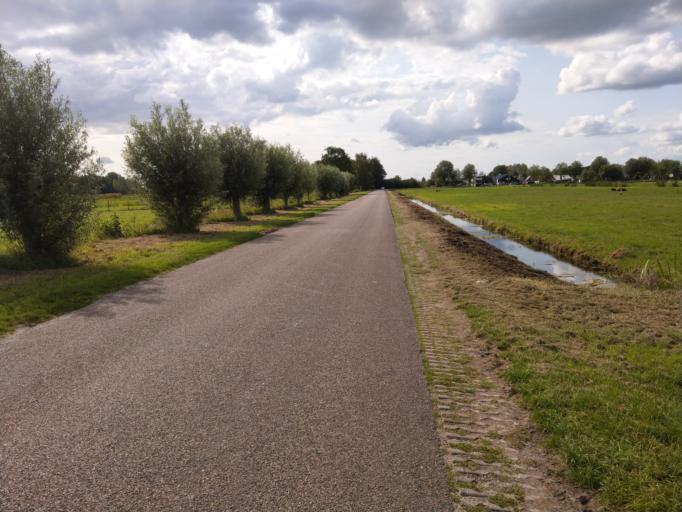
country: NL
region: Overijssel
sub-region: Gemeente Steenwijkerland
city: Giethoorn
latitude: 52.7188
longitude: 6.0843
